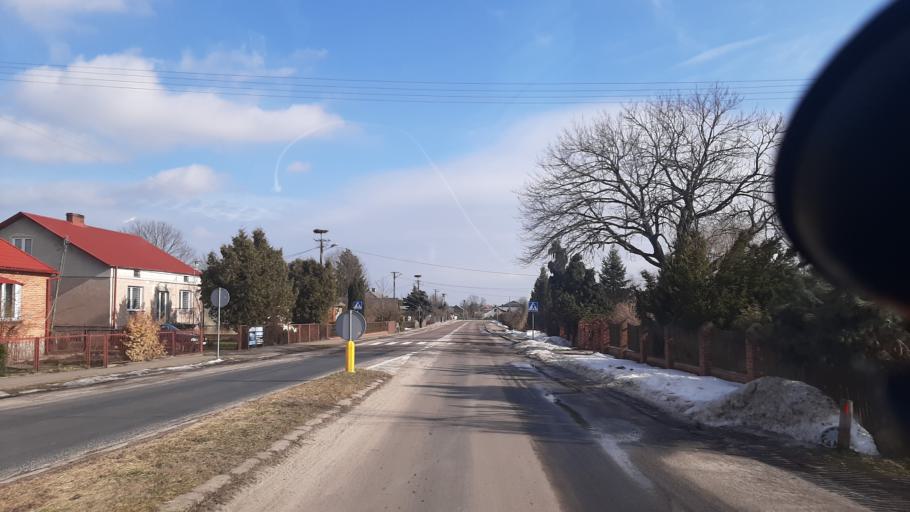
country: PL
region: Lublin Voivodeship
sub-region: Powiat wlodawski
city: Urszulin
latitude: 51.4832
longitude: 23.2848
